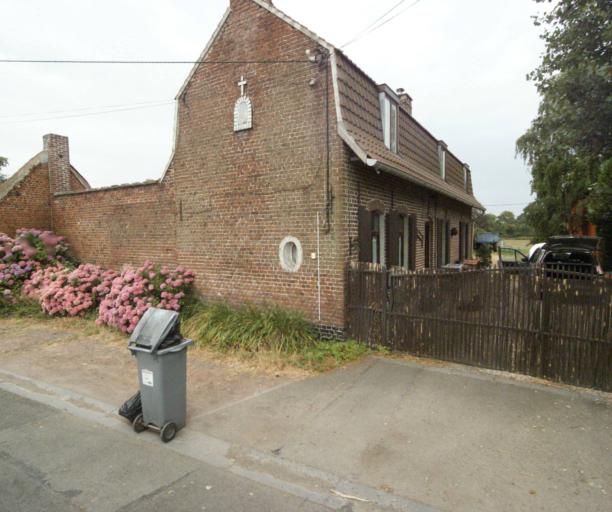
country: FR
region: Nord-Pas-de-Calais
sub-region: Departement du Nord
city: Bondues
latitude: 50.7007
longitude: 3.0783
